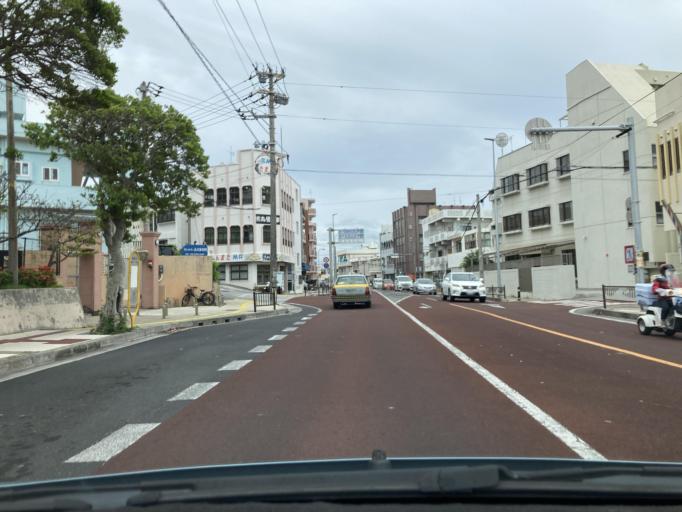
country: JP
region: Okinawa
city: Itoman
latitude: 26.1365
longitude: 127.6702
